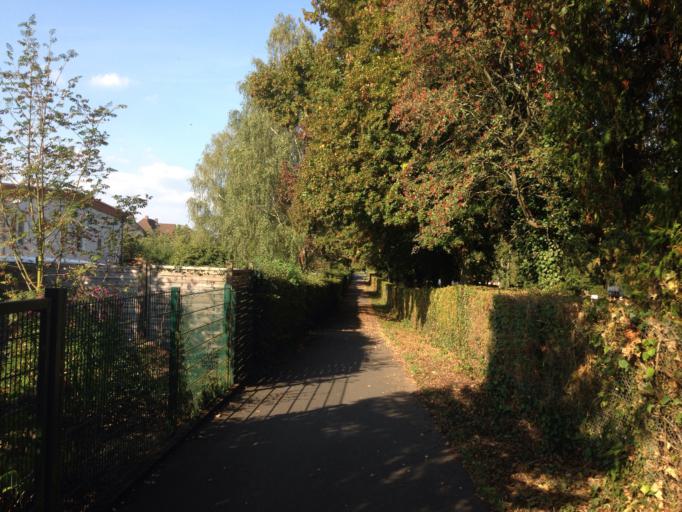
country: DE
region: Hesse
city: Allendorf an der Lahn
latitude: 50.5550
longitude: 8.6485
